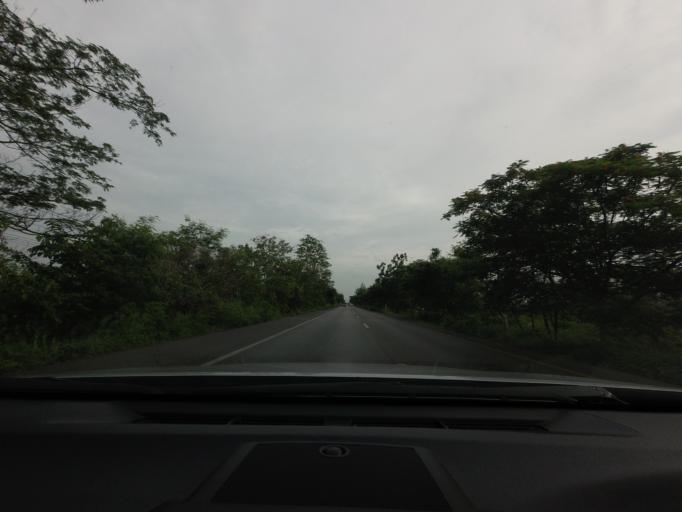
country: TH
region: Phetchaburi
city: Cha-am
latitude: 12.7681
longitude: 99.9352
